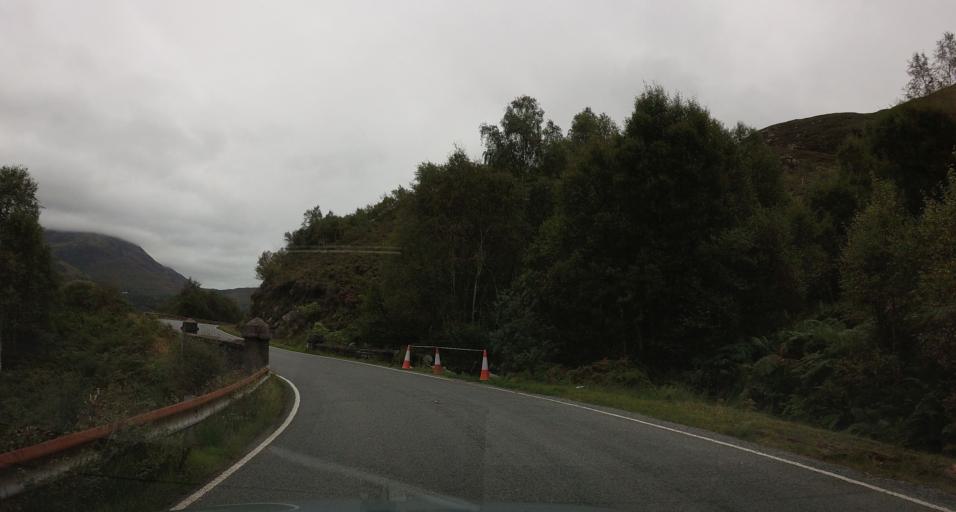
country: GB
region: Scotland
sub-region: Highland
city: Fort William
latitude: 56.7094
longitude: -4.9984
